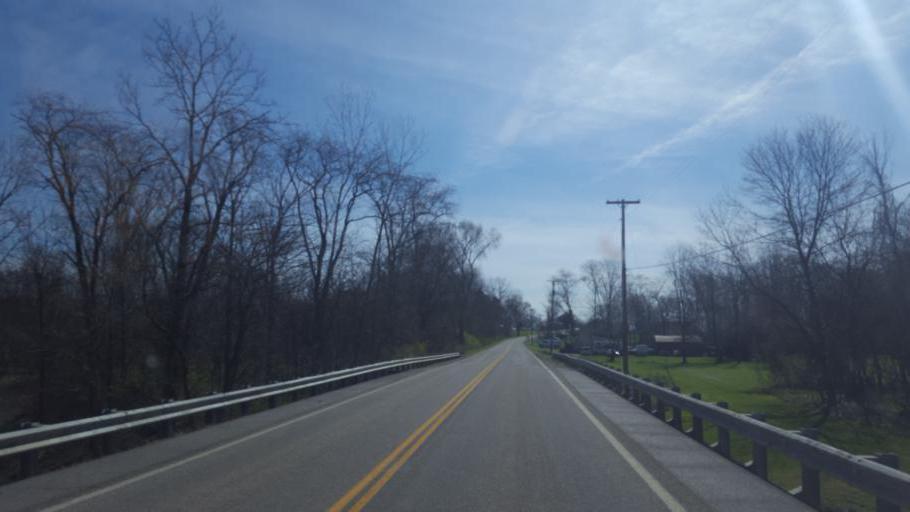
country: US
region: Ohio
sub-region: Delaware County
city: Ashley
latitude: 40.4550
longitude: -82.9603
